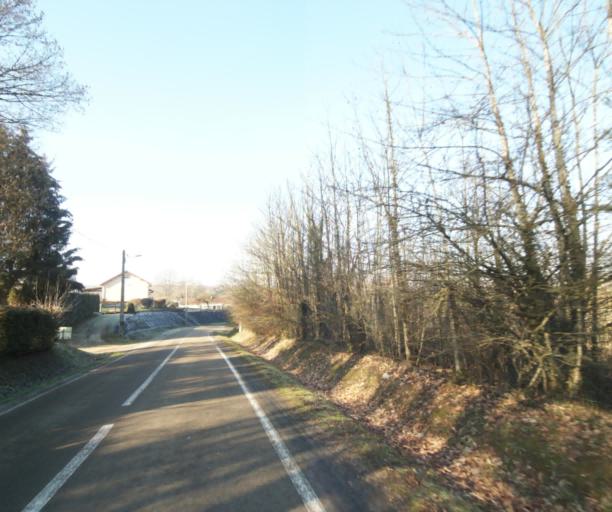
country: FR
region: Champagne-Ardenne
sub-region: Departement de la Haute-Marne
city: Wassy
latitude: 48.4959
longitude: 4.9369
